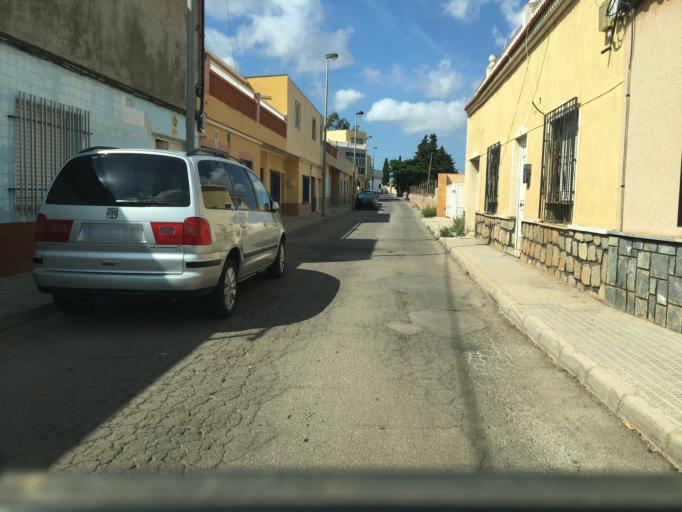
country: ES
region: Murcia
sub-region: Murcia
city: La Union
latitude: 37.6457
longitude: -0.8708
